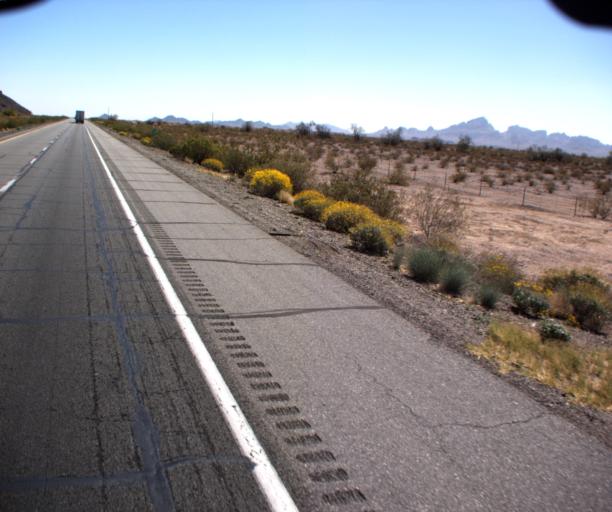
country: US
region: Arizona
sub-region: La Paz County
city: Salome
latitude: 33.5309
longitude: -113.1267
